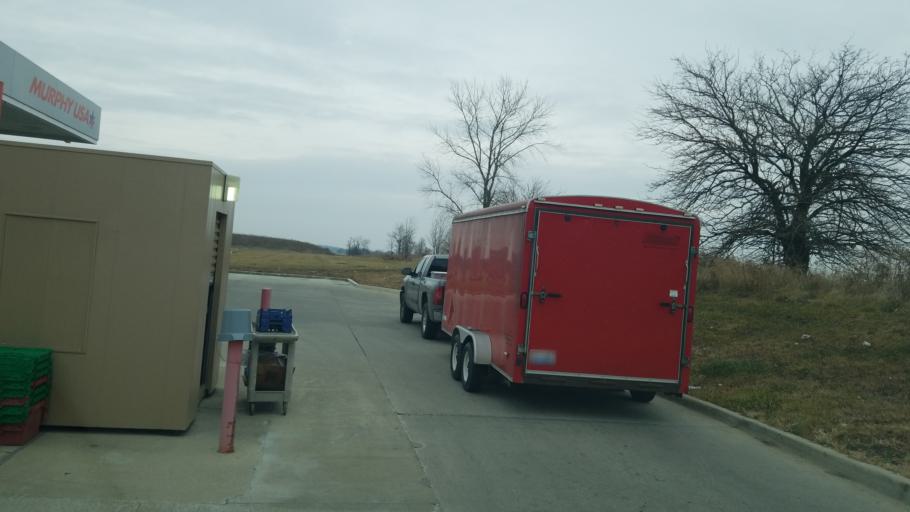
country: US
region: Ohio
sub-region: Hardin County
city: Kenton
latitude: 40.6572
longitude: -83.5833
